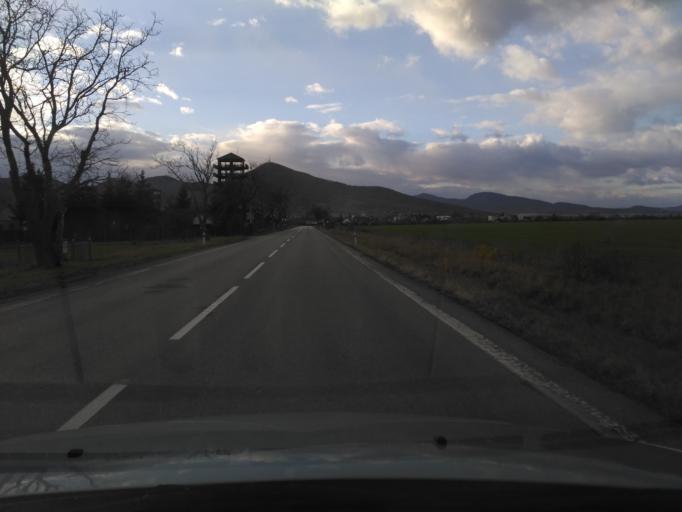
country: HU
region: Borsod-Abauj-Zemplen
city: Satoraljaujhely
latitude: 48.3975
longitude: 21.6862
